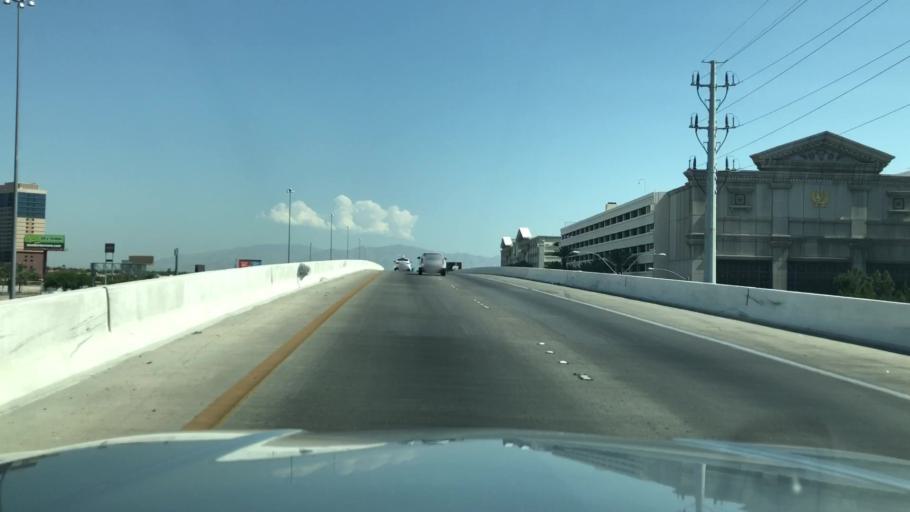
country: US
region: Nevada
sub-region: Clark County
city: Paradise
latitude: 36.1162
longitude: -115.1802
